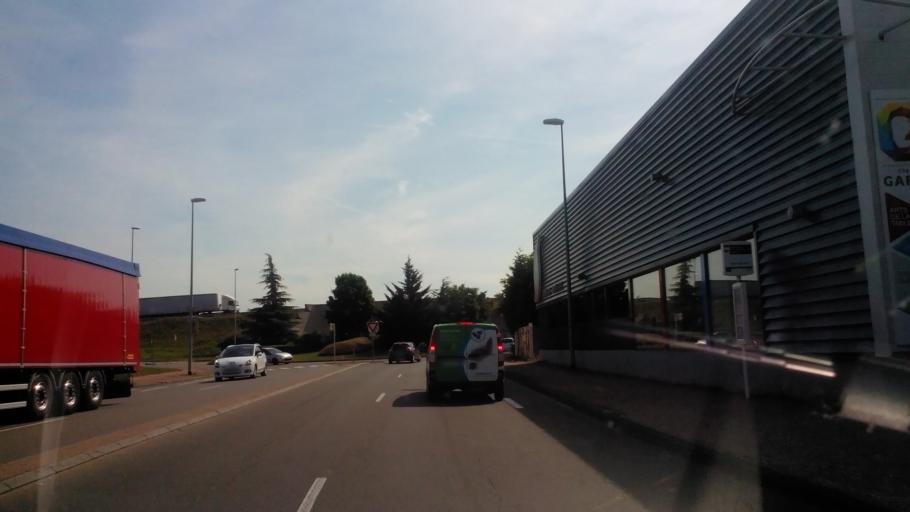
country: FR
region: Bourgogne
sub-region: Departement de la Cote-d'Or
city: Saint-Apollinaire
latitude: 47.3397
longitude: 5.0682
